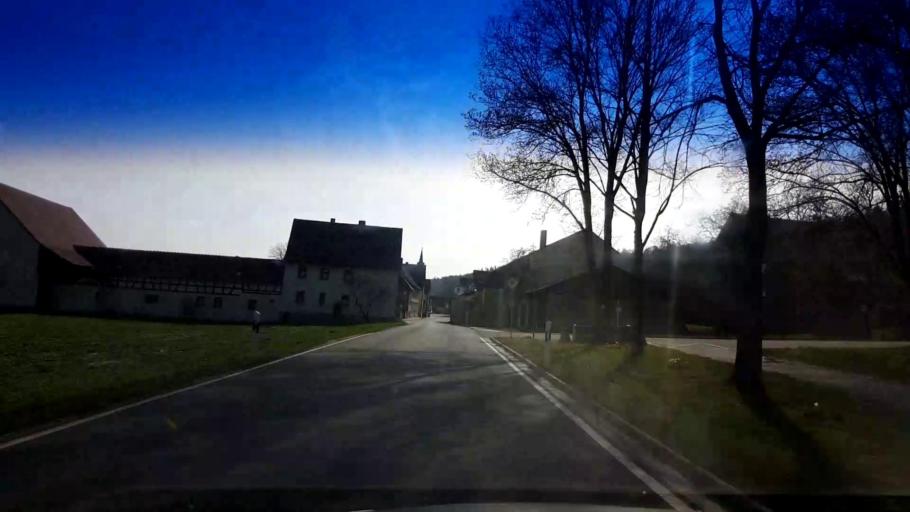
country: DE
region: Bavaria
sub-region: Upper Franconia
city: Ebensfeld
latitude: 50.0525
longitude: 10.9292
